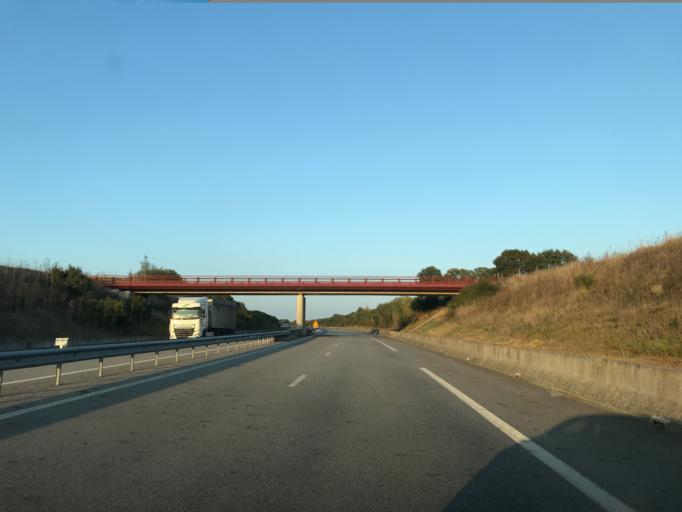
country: FR
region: Lower Normandy
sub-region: Departement de l'Orne
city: Sees
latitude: 48.4900
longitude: 0.2923
